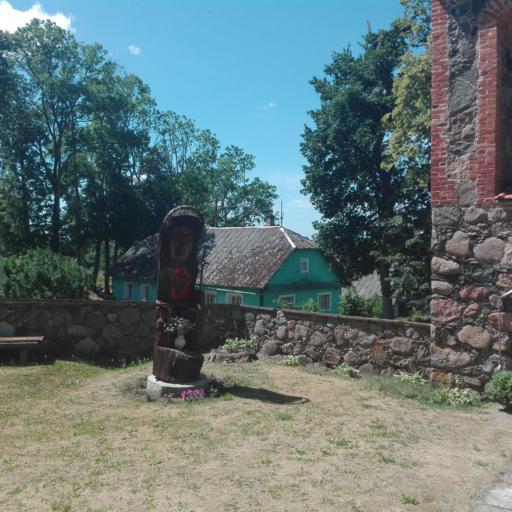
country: LT
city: Kupiskis
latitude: 55.9395
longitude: 24.8860
